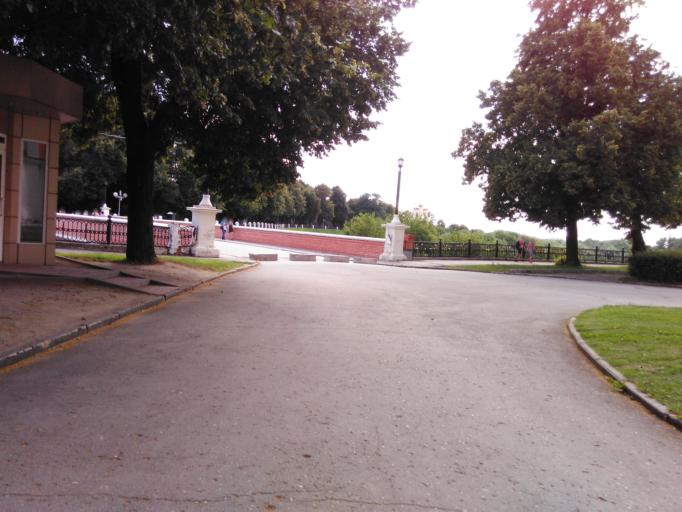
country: RU
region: Rjazan
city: Ryazan'
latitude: 54.6353
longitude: 39.7478
